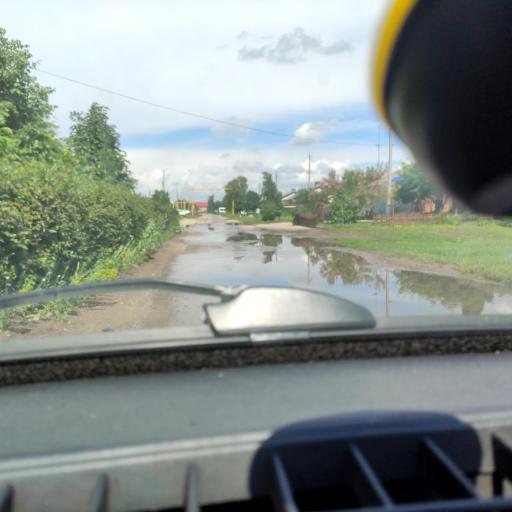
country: RU
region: Samara
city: Zhigulevsk
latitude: 53.5519
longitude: 49.5202
